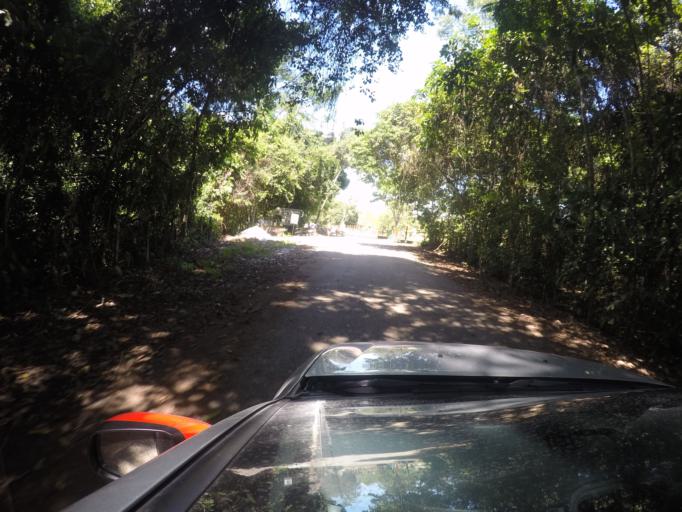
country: CO
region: Antioquia
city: Puerto Triunfo
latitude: 5.9238
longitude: -74.7230
